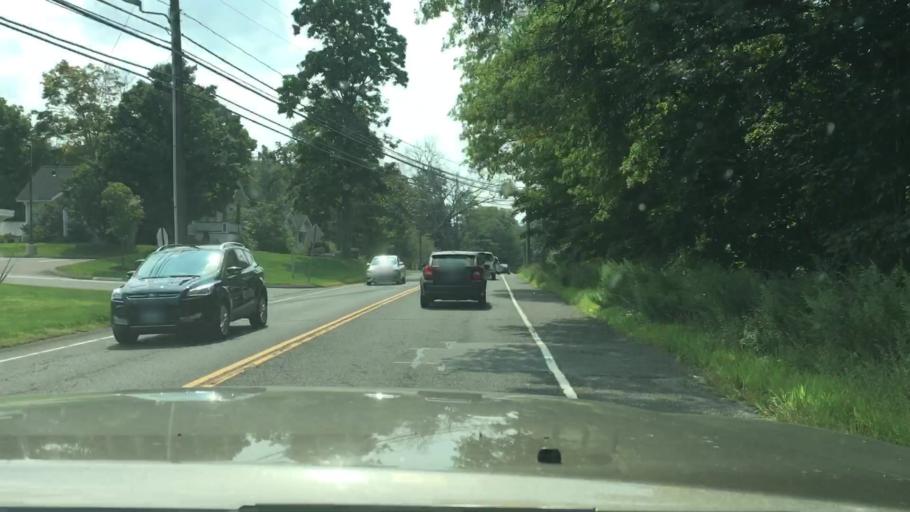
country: US
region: Connecticut
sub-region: New Haven County
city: Cheshire Village
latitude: 41.5215
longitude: -72.9317
